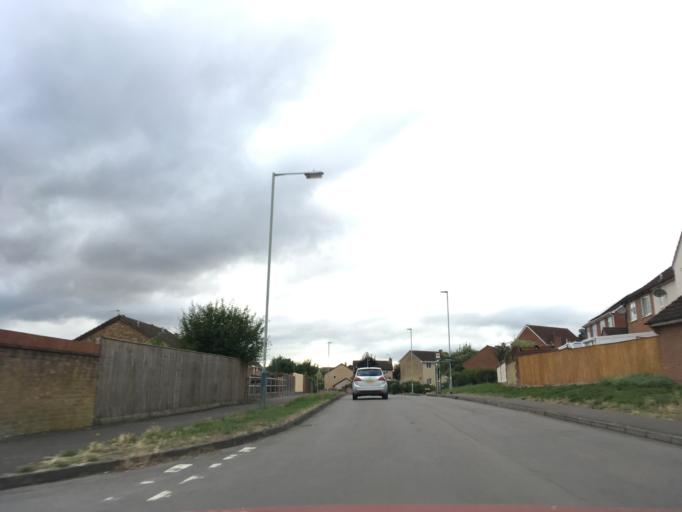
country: GB
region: England
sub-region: Wiltshire
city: Chippenham
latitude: 51.4480
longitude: -2.0993
